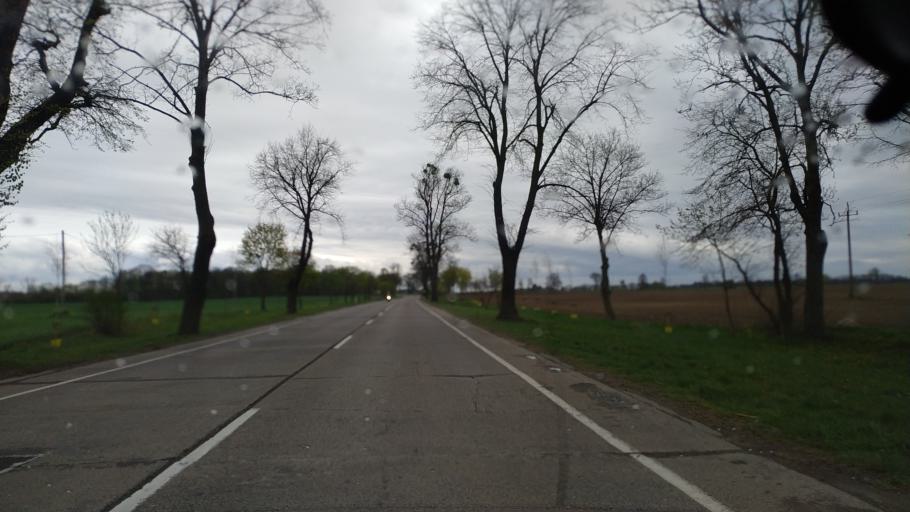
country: PL
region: Pomeranian Voivodeship
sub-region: Powiat starogardzki
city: Zblewo
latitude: 53.9317
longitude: 18.3654
